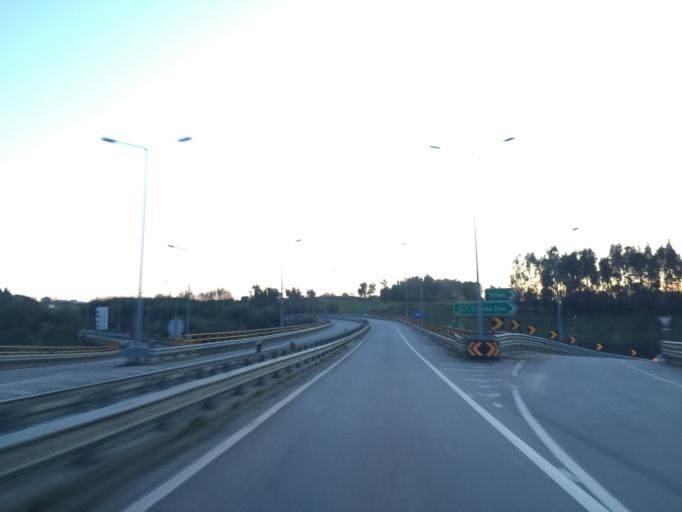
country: PT
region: Viseu
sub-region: Santa Comba Dao
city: Santa Comba Dao
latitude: 40.3843
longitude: -8.1165
